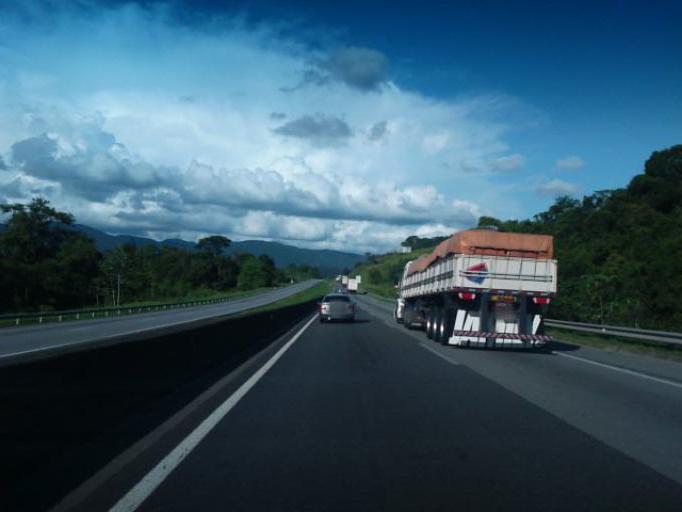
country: BR
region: Sao Paulo
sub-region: Miracatu
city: Miracatu
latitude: -24.1797
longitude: -47.3505
